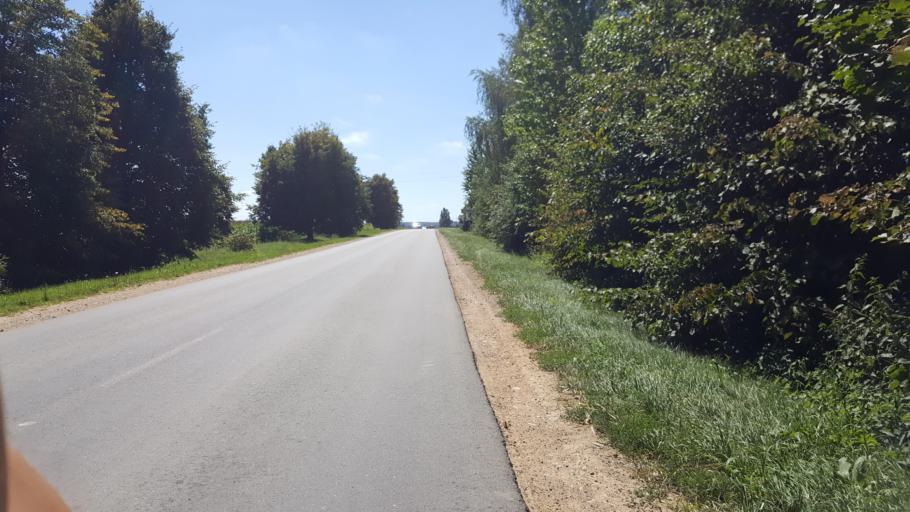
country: BY
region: Brest
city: Charnawchytsy
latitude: 52.2841
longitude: 23.6037
